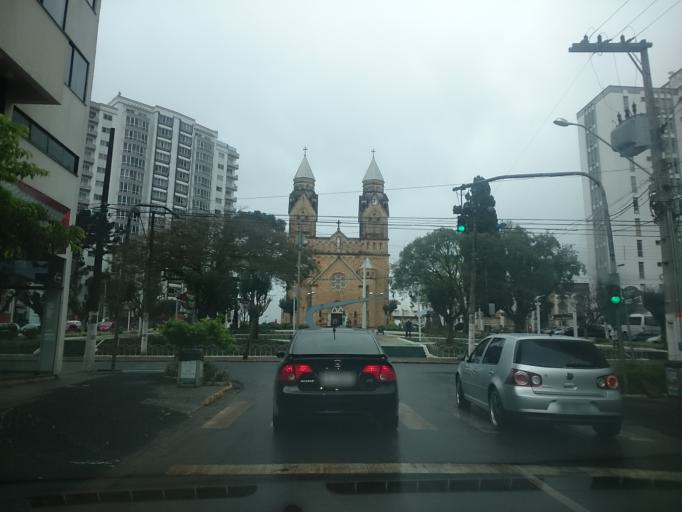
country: BR
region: Santa Catarina
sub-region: Lages
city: Lages
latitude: -27.8161
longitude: -50.3262
